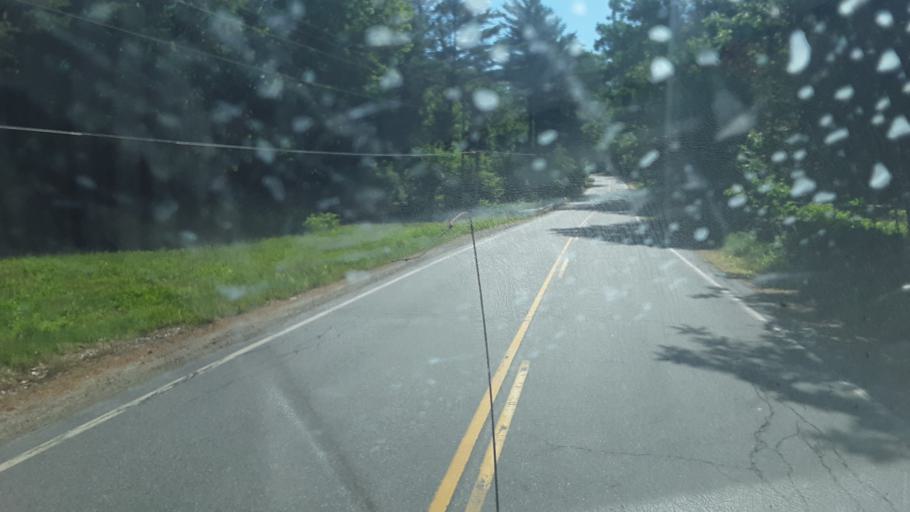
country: US
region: New Hampshire
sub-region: Grafton County
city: North Haverhill
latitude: 44.0869
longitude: -71.9576
